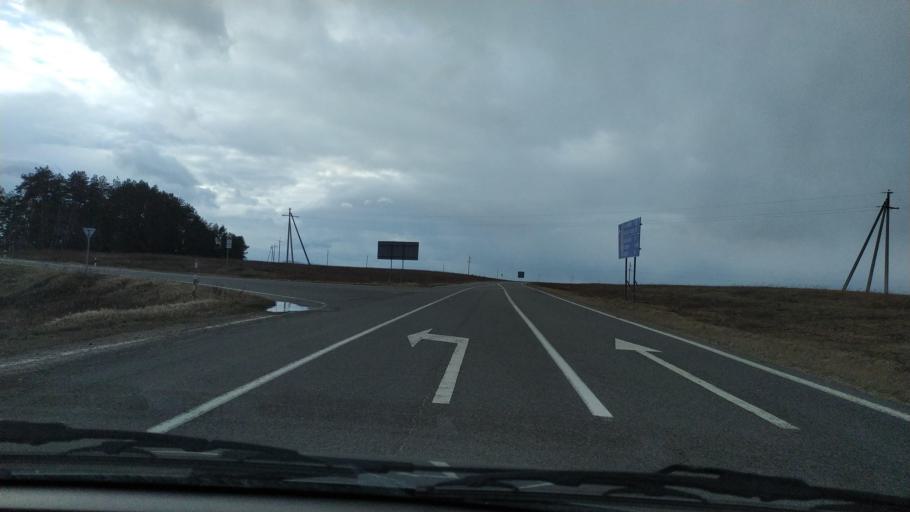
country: BY
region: Brest
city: Kamyanyets
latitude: 52.4033
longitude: 23.8667
